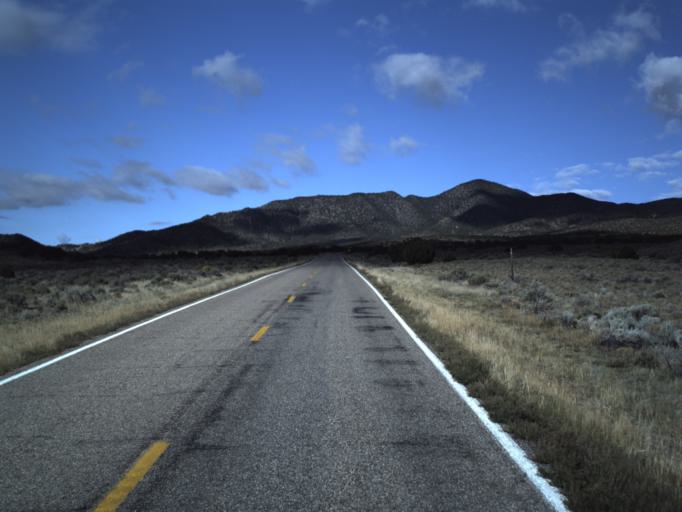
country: US
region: Utah
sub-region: Beaver County
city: Milford
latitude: 38.4613
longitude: -113.2400
